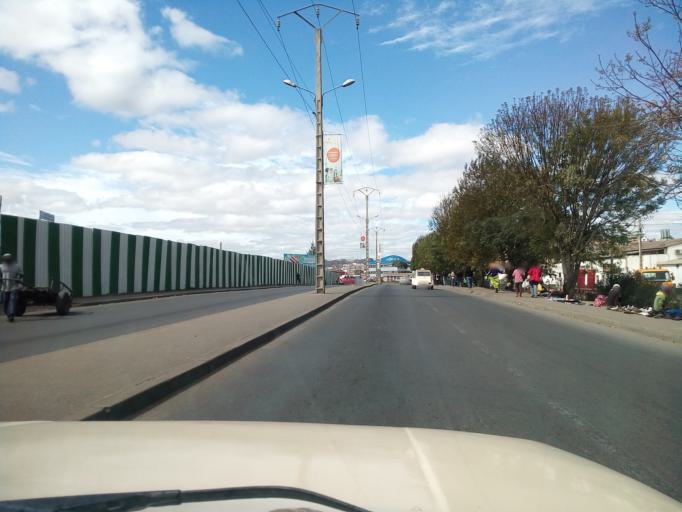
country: MG
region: Analamanga
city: Antananarivo
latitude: -18.8932
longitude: 47.5204
